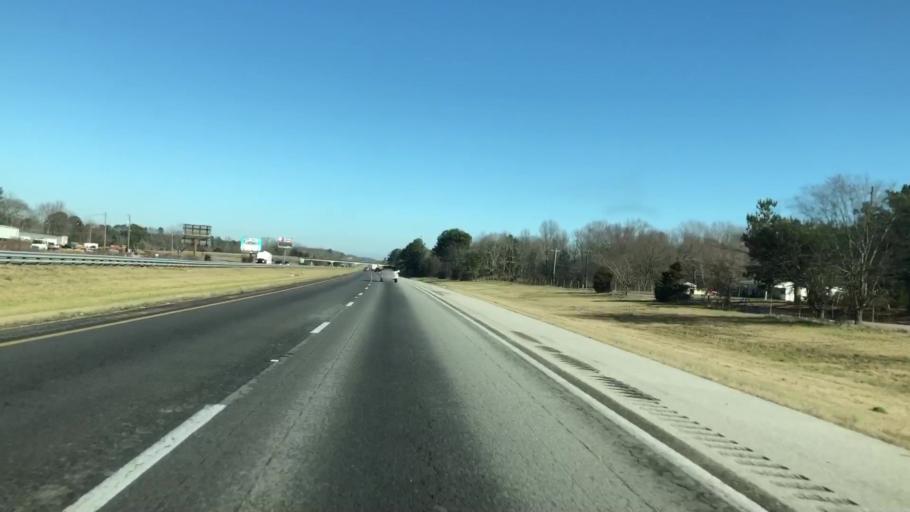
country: US
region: Alabama
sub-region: Limestone County
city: Athens
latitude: 34.8551
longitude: -86.9282
